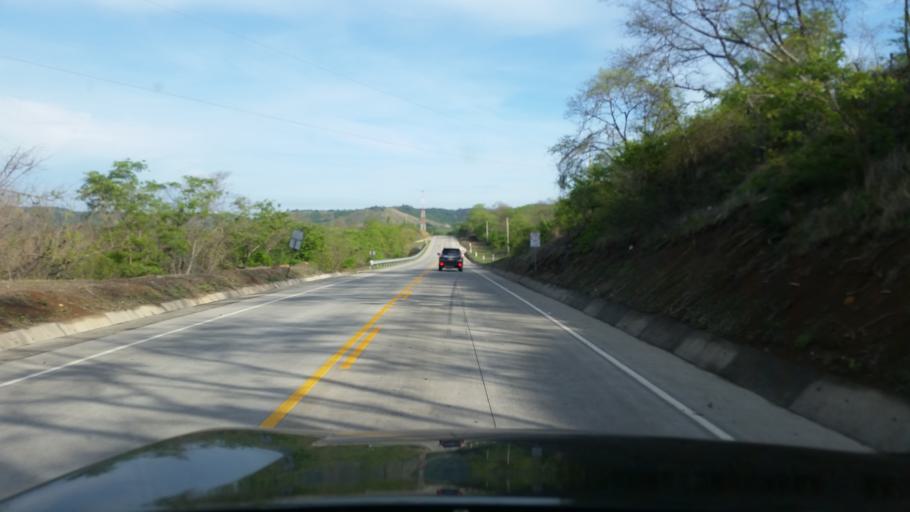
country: NI
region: Leon
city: Nagarote
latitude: 12.1279
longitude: -86.6374
